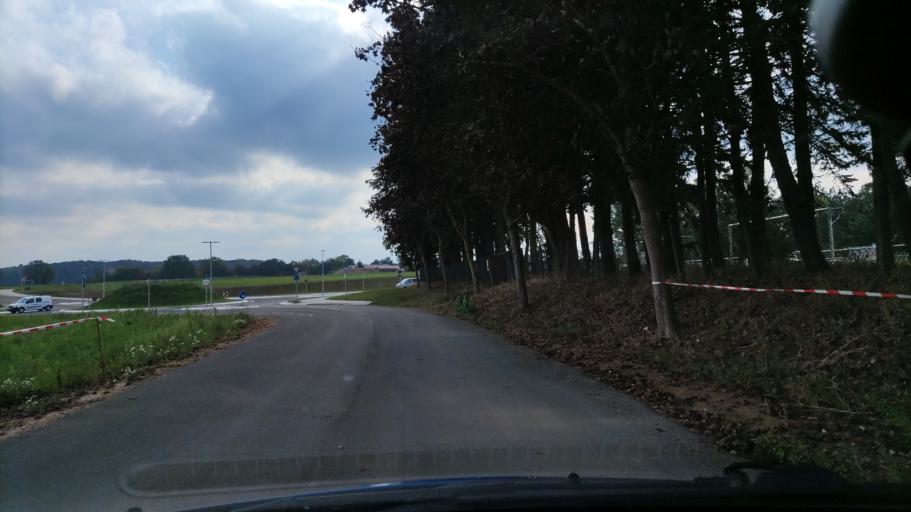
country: DE
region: Lower Saxony
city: Neetze
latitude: 53.2678
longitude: 10.6330
